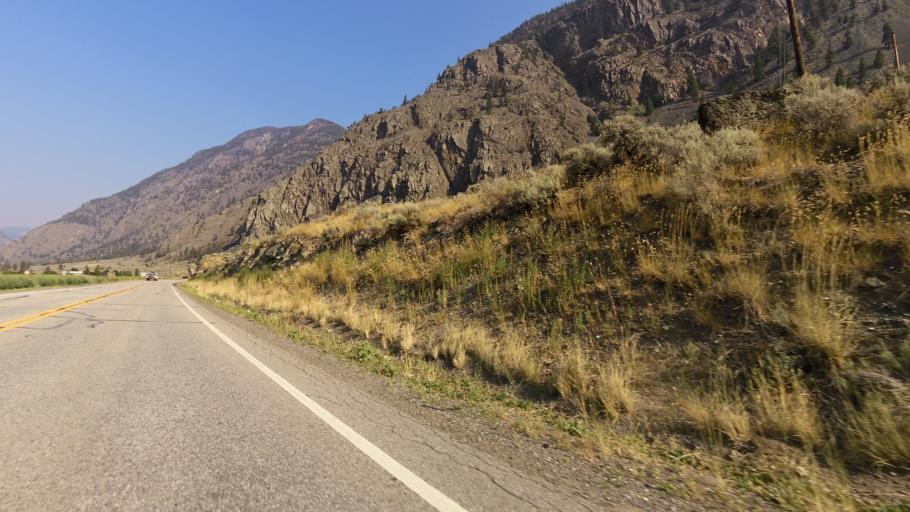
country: CA
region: British Columbia
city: Oliver
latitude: 49.2152
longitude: -119.9101
